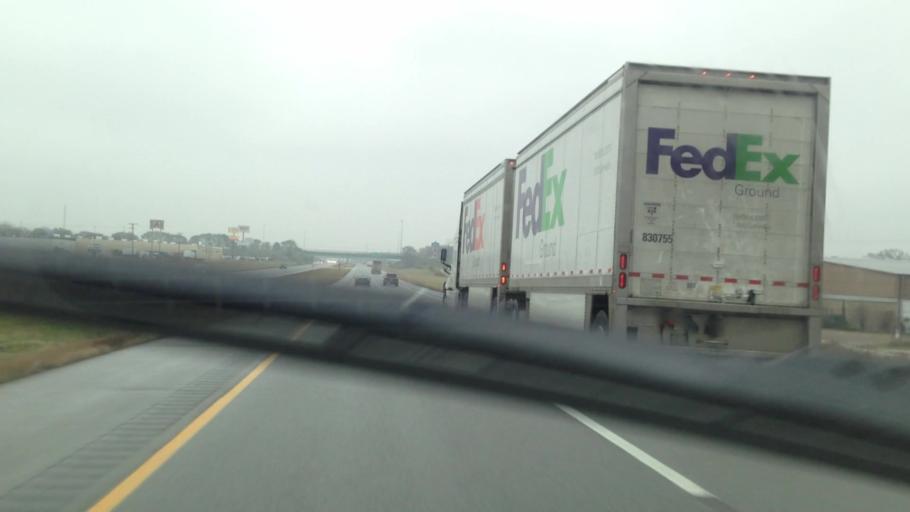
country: US
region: Indiana
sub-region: Elkhart County
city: Simonton Lake
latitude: 41.7312
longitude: -85.9820
